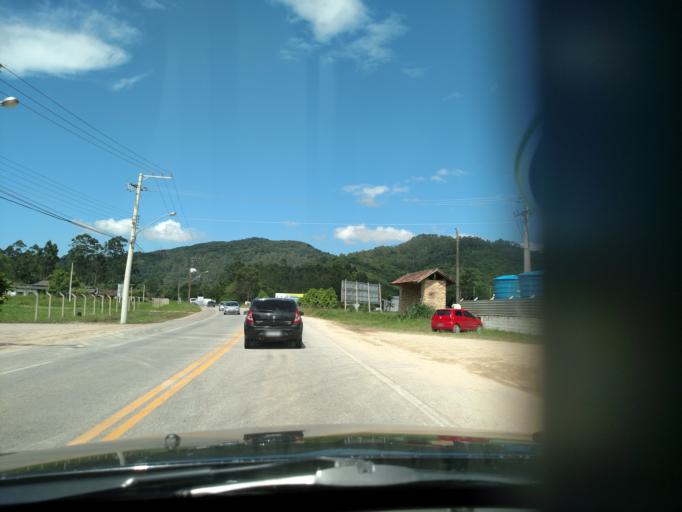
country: BR
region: Santa Catarina
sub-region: Itajai
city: Itajai
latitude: -26.8921
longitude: -48.7711
